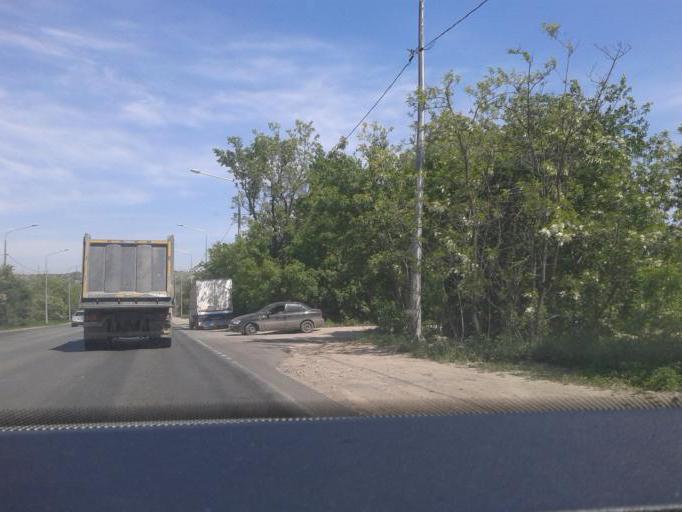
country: RU
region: Volgograd
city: Gorodishche
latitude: 48.7920
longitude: 44.5208
